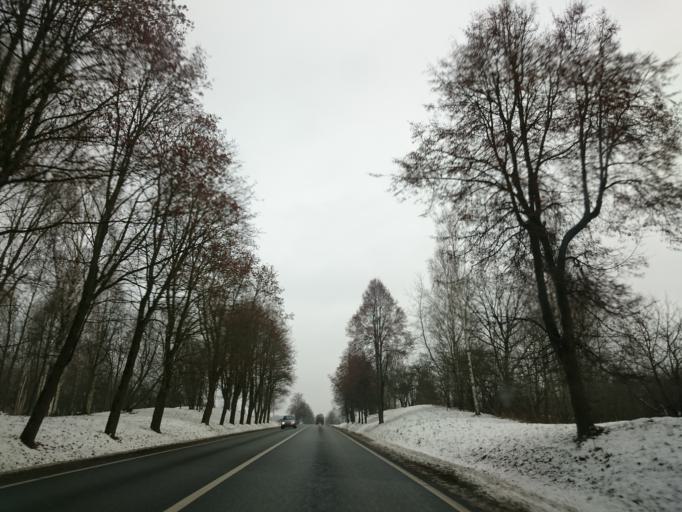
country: LV
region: Krimulda
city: Ragana
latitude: 57.1683
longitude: 24.7012
